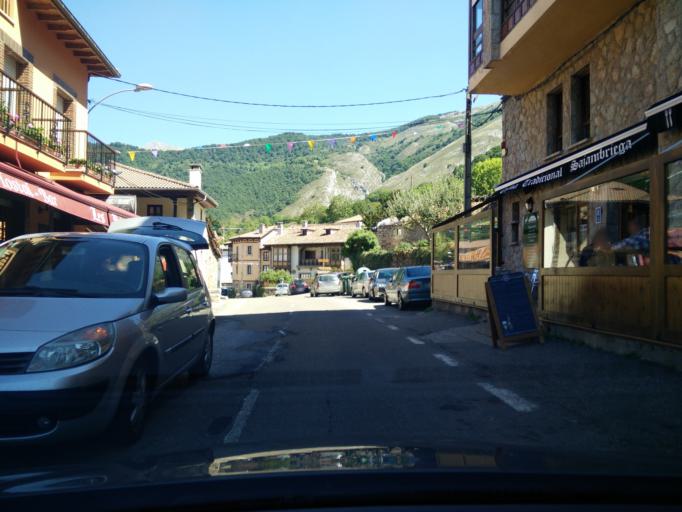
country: ES
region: Castille and Leon
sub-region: Provincia de Leon
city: Oseja de Sajambre
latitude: 43.1349
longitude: -5.0378
